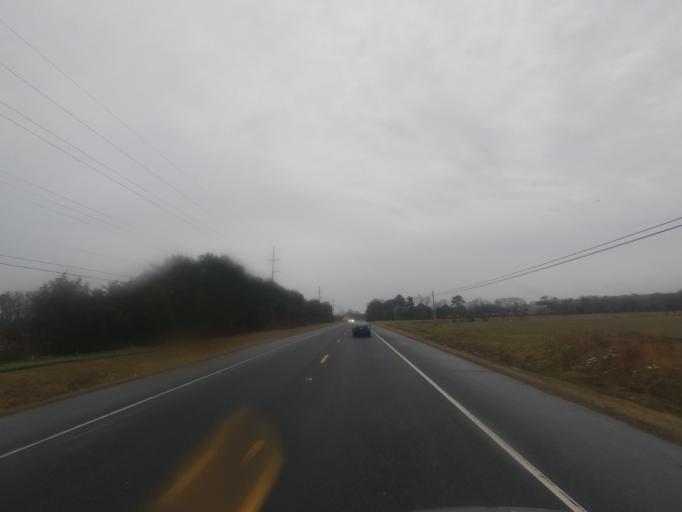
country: US
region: Maryland
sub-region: Dorchester County
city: Hurlock
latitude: 38.5844
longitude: -75.9611
